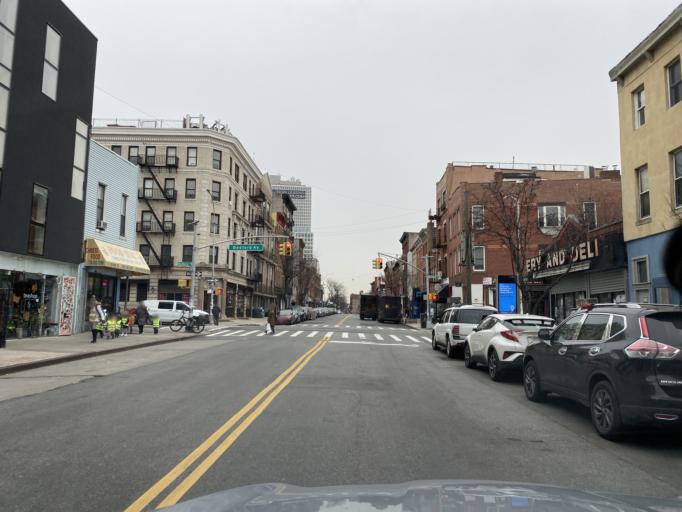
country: US
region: New York
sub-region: Queens County
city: Long Island City
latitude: 40.7144
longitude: -73.9609
